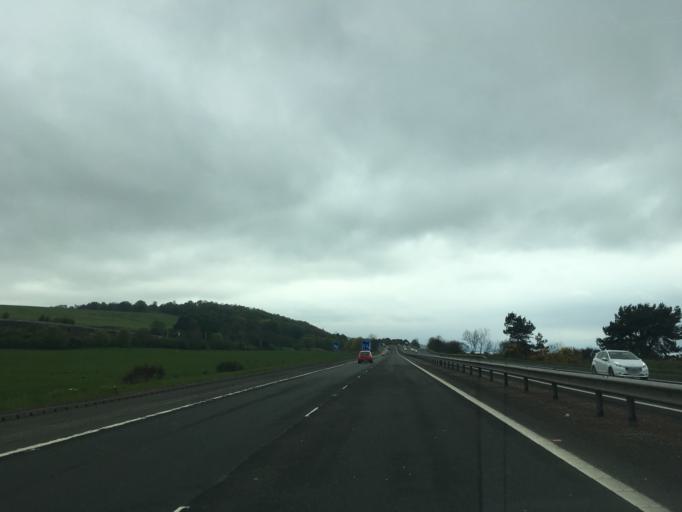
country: GB
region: Scotland
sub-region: West Dunbartonshire
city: Dumbarton
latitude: 55.9231
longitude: -4.5439
